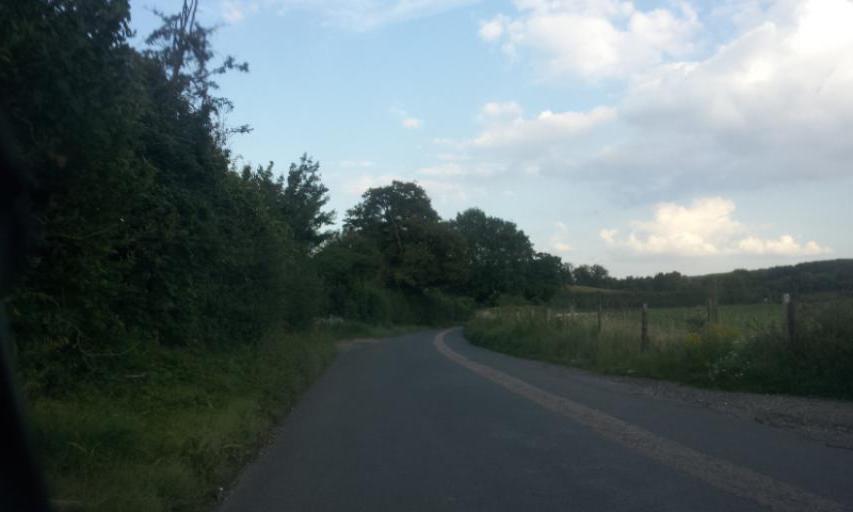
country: GB
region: England
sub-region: Medway
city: Cuxton
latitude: 51.3802
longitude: 0.4214
